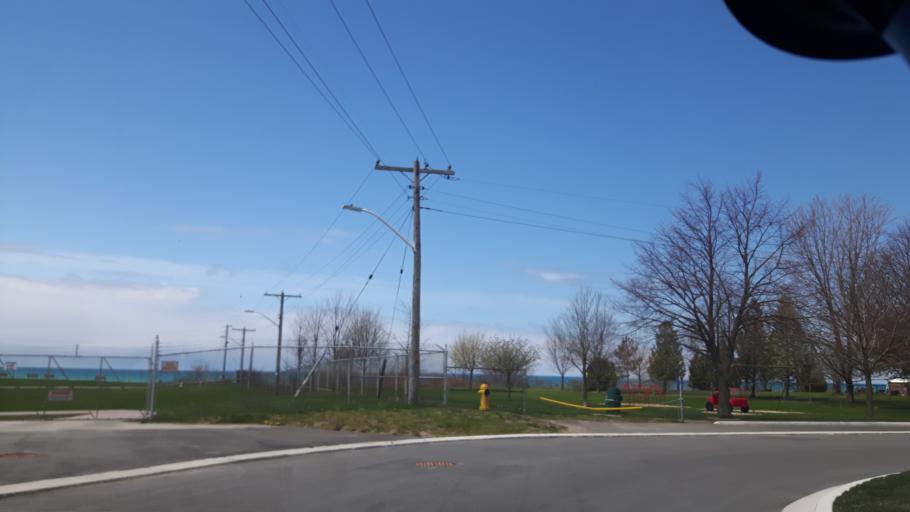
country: CA
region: Ontario
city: Goderich
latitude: 43.7316
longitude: -81.7226
